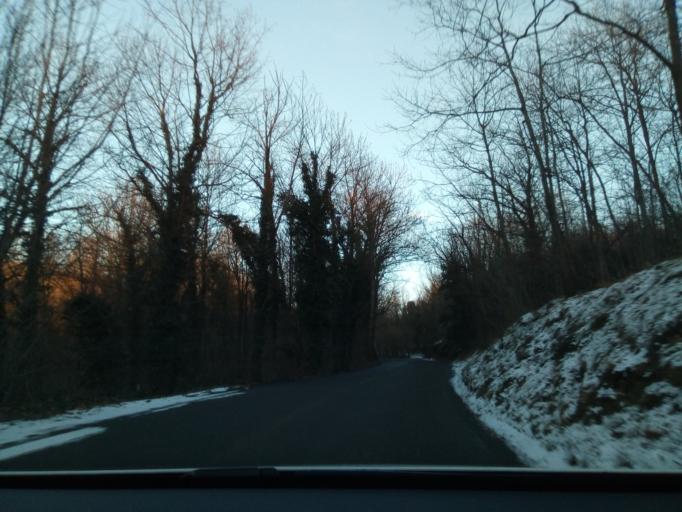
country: IT
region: Piedmont
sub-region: Provincia di Torino
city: Cascinette d'Ivrea
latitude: 45.4895
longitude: 7.9061
